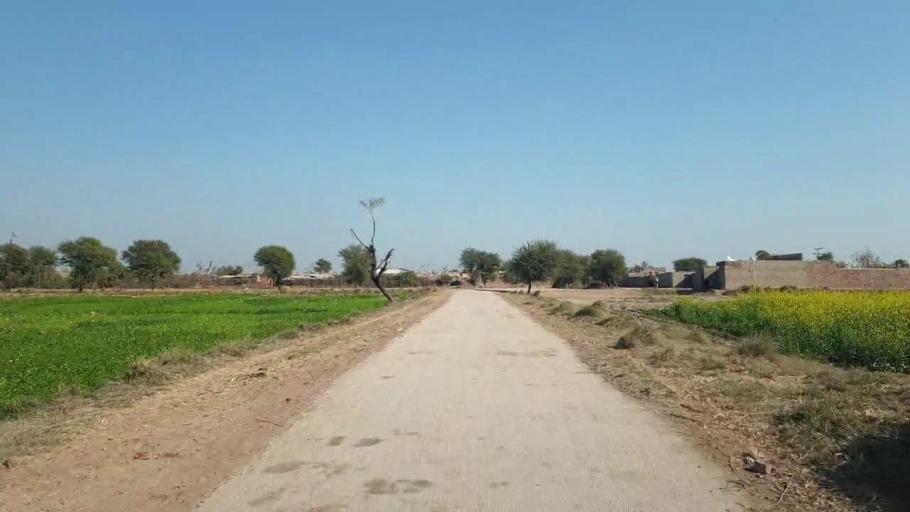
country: PK
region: Sindh
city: Shahdadpur
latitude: 25.9785
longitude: 68.6653
